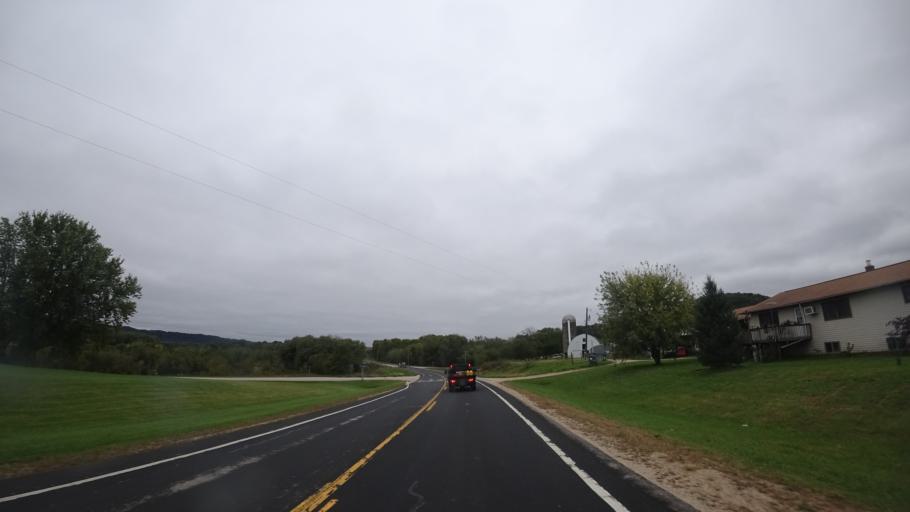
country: US
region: Wisconsin
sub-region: Grant County
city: Boscobel
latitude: 43.1113
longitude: -90.8017
